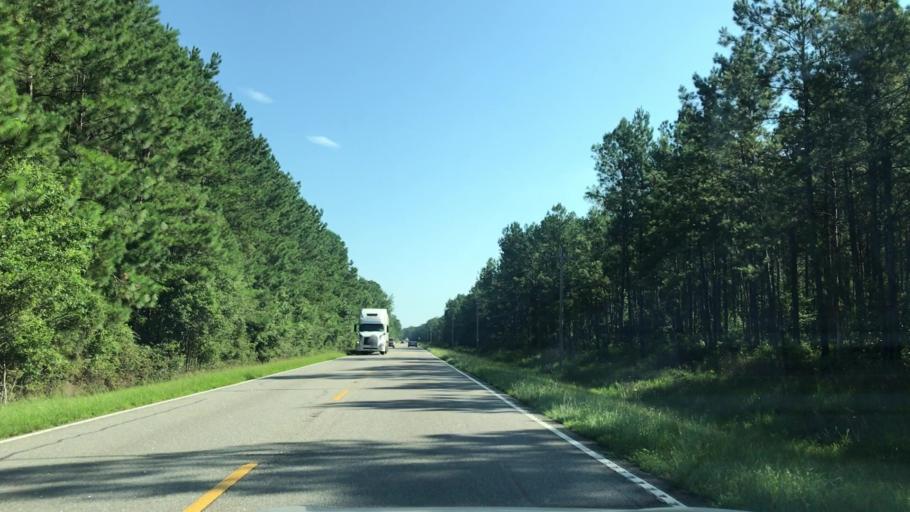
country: US
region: South Carolina
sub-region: Georgetown County
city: Georgetown
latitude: 33.4990
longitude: -79.2597
